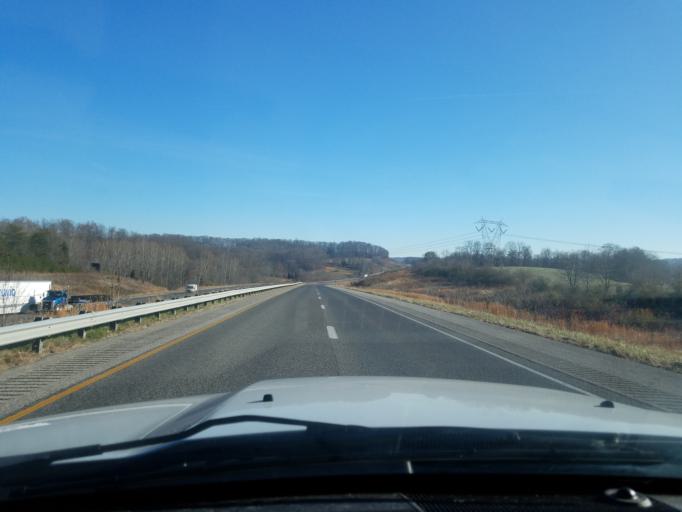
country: US
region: Indiana
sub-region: Dubois County
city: Ferdinand
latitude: 38.2145
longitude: -86.7436
